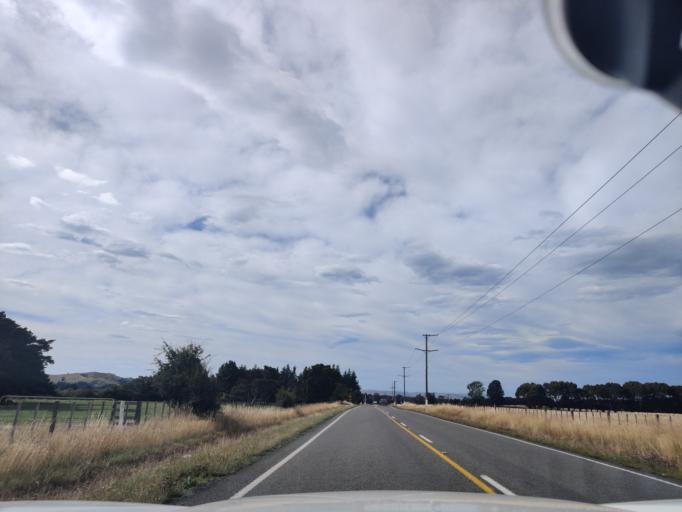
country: NZ
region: Wellington
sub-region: Masterton District
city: Masterton
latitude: -40.8398
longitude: 175.6305
